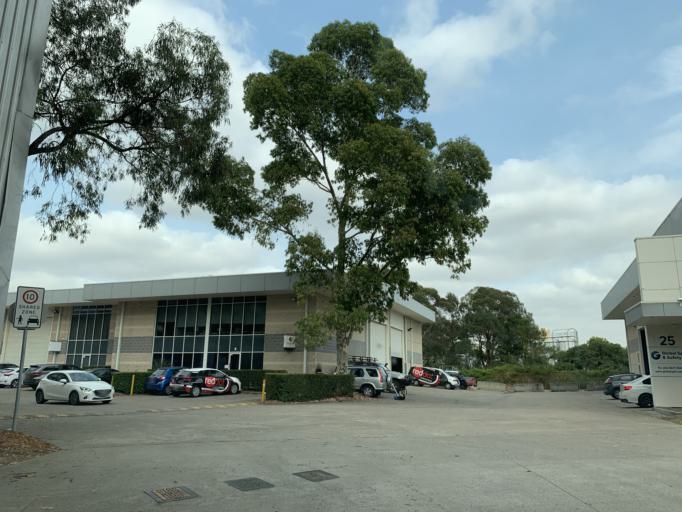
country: AU
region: New South Wales
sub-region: Holroyd
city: Girraween
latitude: -33.7730
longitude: 150.9524
